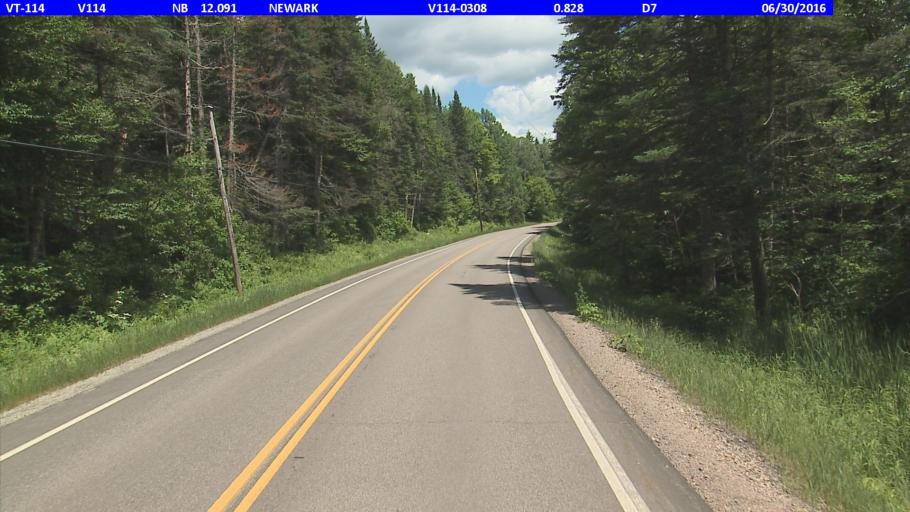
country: US
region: Vermont
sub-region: Caledonia County
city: Lyndonville
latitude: 44.6807
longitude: -71.8807
